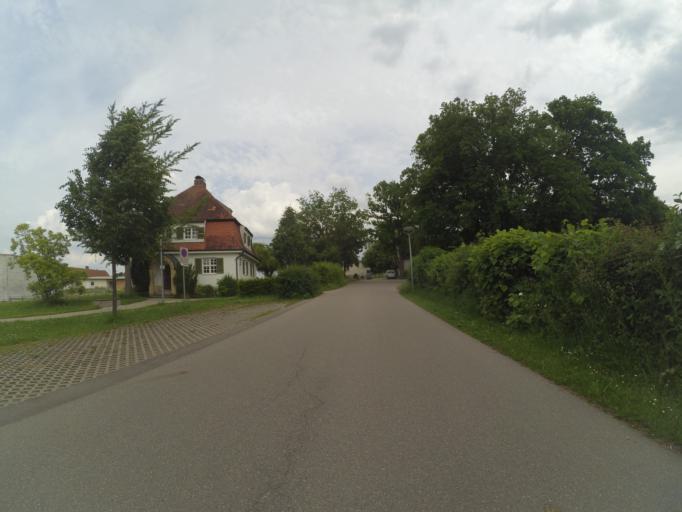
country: DE
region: Bavaria
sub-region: Swabia
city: Guenzburg
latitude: 48.4601
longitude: 10.2947
